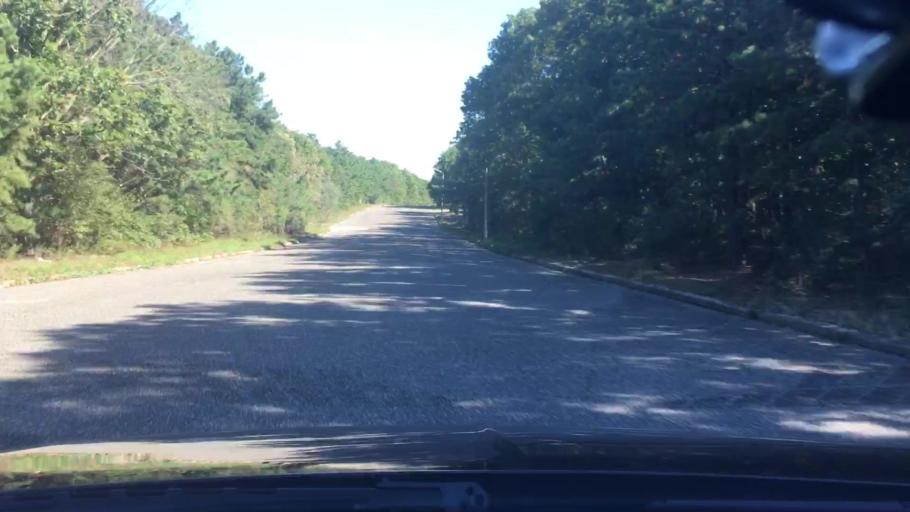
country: US
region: New York
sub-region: Suffolk County
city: Yaphank
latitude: 40.8473
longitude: -72.8786
